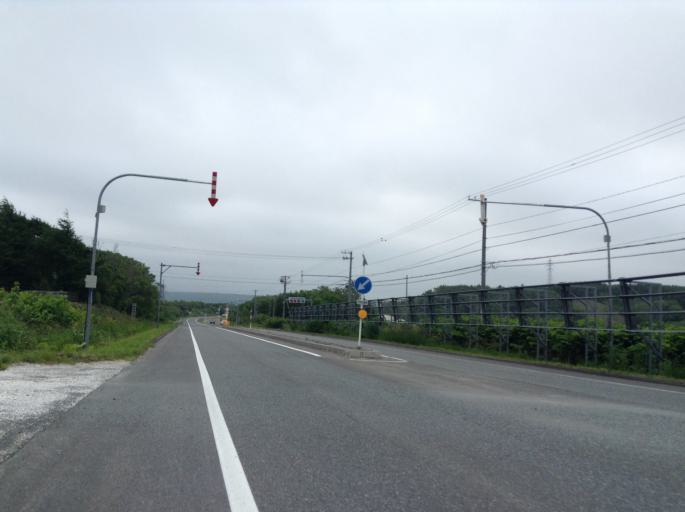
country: JP
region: Hokkaido
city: Wakkanai
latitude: 45.3709
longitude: 141.7225
